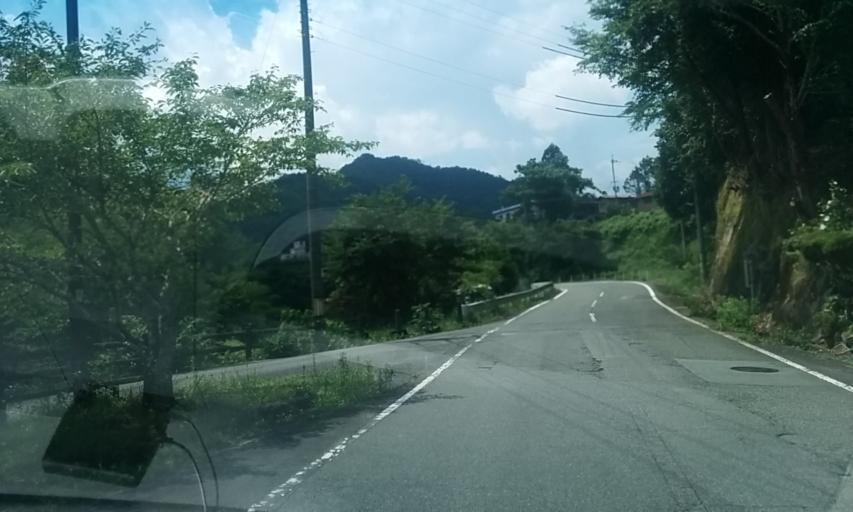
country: JP
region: Hyogo
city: Sasayama
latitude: 35.1701
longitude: 135.2745
